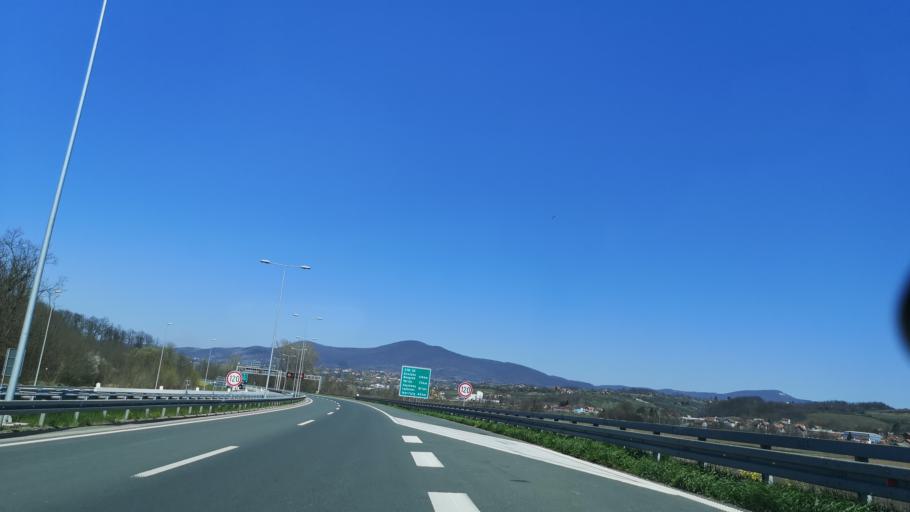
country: RS
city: Prislonica
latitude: 43.9227
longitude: 20.3984
